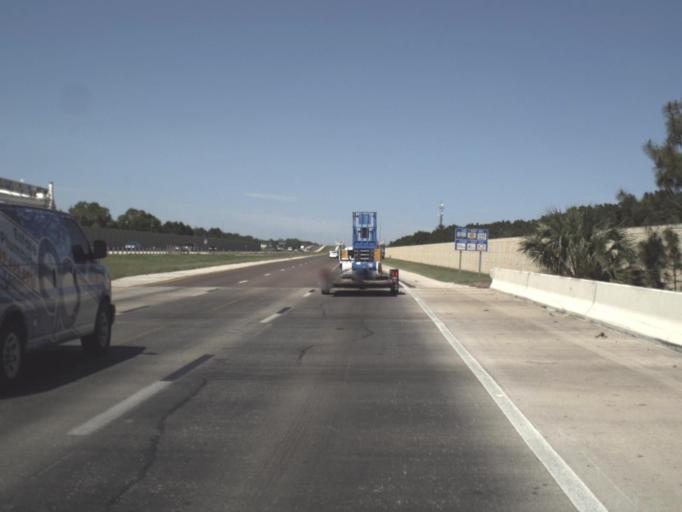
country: US
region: Florida
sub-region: Lee County
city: Estero
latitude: 26.4214
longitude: -81.7737
